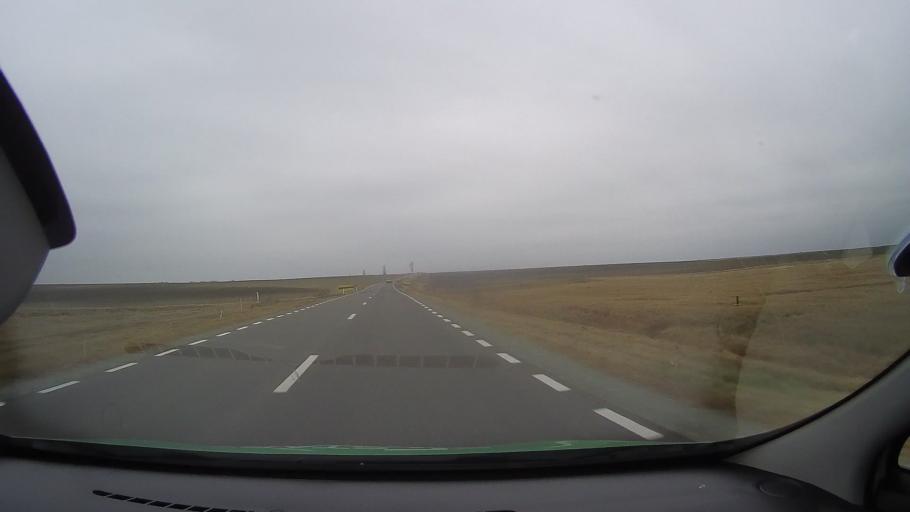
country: RO
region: Ialomita
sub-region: Comuna Scanteia
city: Iazu
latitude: 44.7215
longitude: 27.4219
